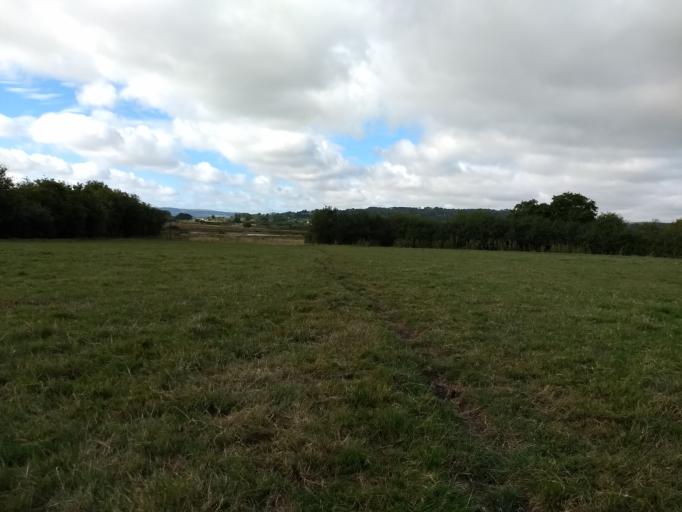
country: GB
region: England
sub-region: Isle of Wight
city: Brading
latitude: 50.6915
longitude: -1.1259
